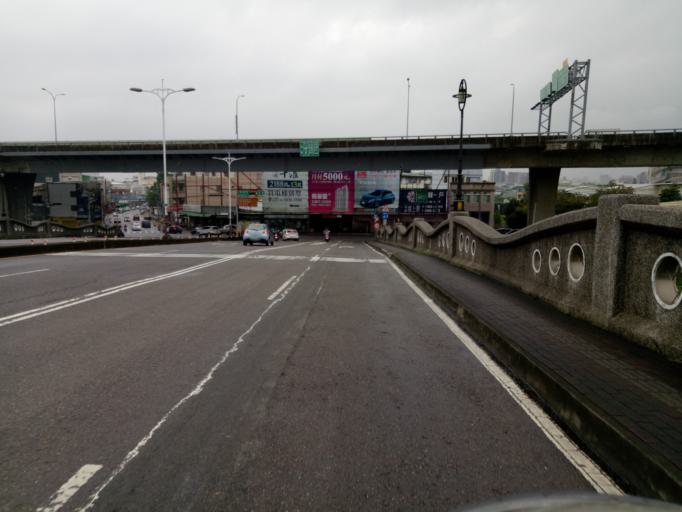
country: TW
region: Taiwan
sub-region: Taichung City
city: Taichung
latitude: 24.1110
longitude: 120.6978
